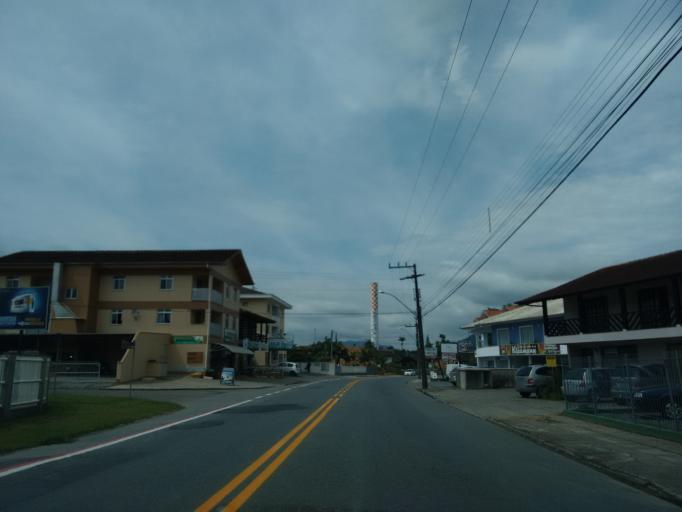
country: BR
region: Santa Catarina
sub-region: Pomerode
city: Pomerode
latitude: -26.7031
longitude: -49.1618
